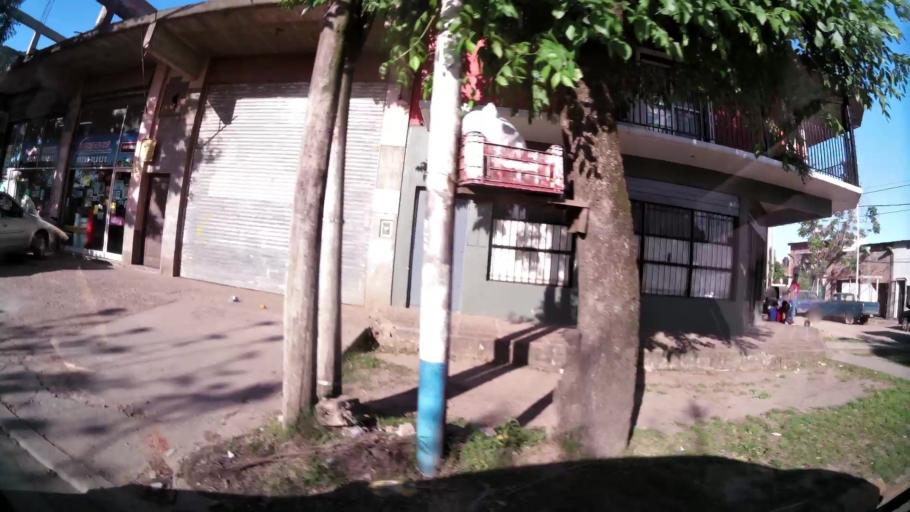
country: AR
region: Buenos Aires
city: Santa Catalina - Dique Lujan
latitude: -34.4941
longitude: -58.7205
